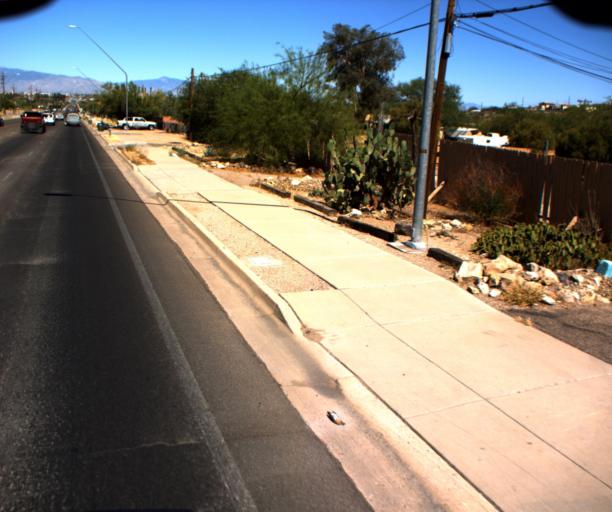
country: US
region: Arizona
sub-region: Pima County
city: Drexel Heights
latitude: 32.1779
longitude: -111.0099
